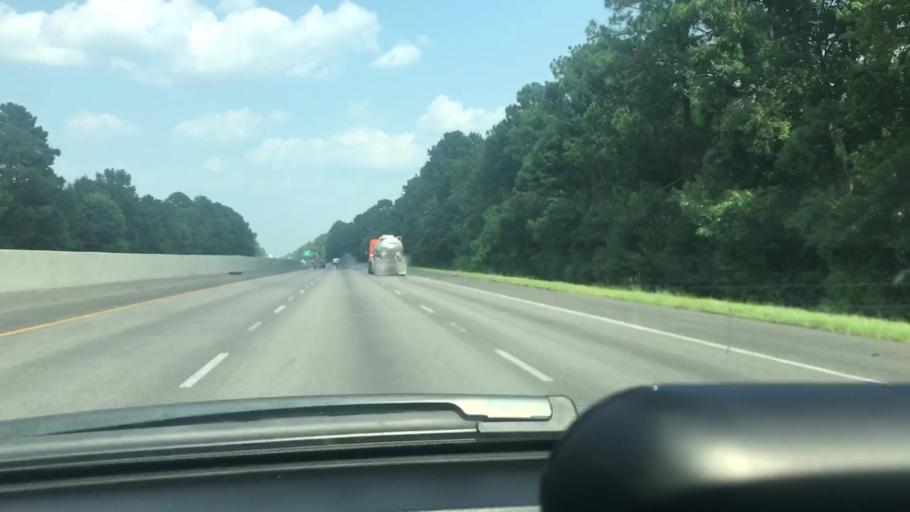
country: US
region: Louisiana
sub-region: Livingston Parish
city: Walker
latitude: 30.4665
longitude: -90.8912
